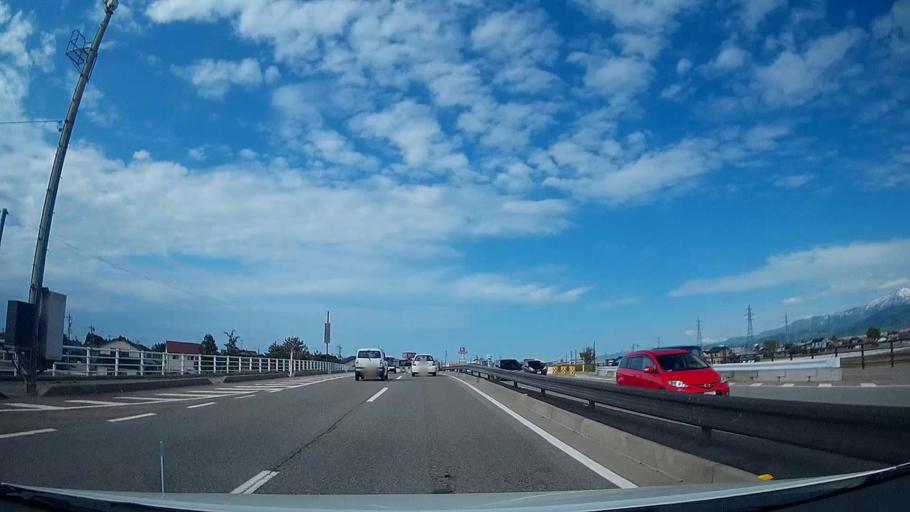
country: JP
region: Toyama
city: Namerikawa
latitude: 36.7536
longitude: 137.3570
